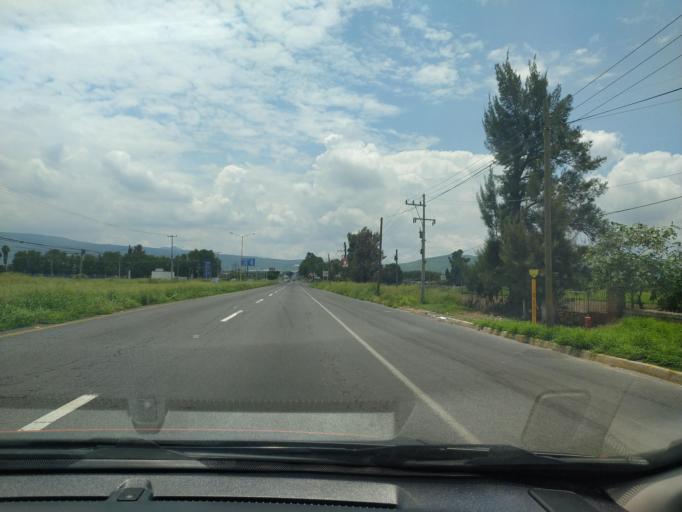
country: MX
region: Jalisco
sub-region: Tlajomulco de Zuniga
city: Santa Cruz de las Flores
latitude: 20.4737
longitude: -103.5019
